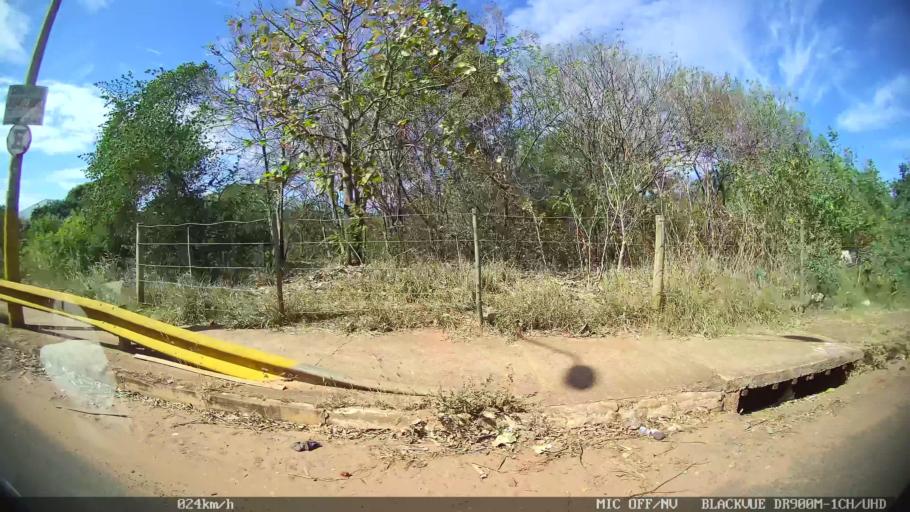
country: BR
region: Sao Paulo
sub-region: Bady Bassitt
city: Bady Bassitt
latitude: -20.8264
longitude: -49.4942
